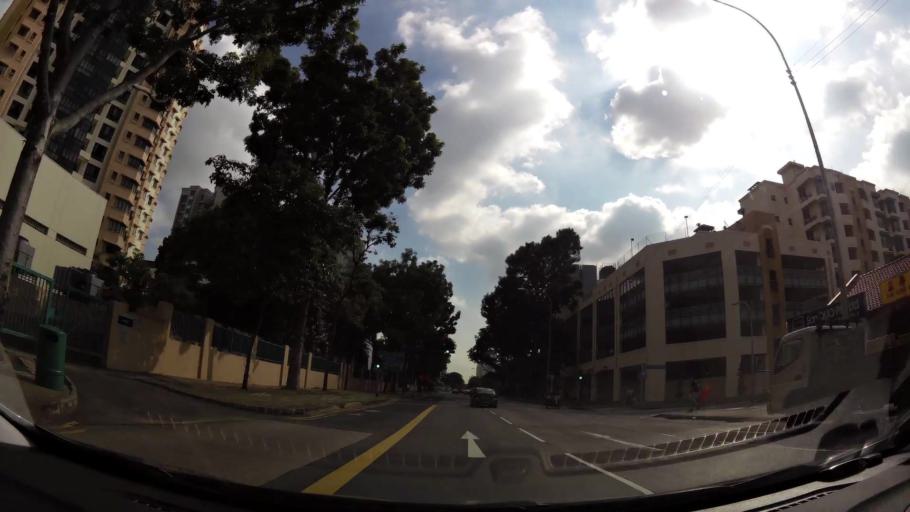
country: SG
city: Singapore
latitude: 1.3166
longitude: 103.8904
